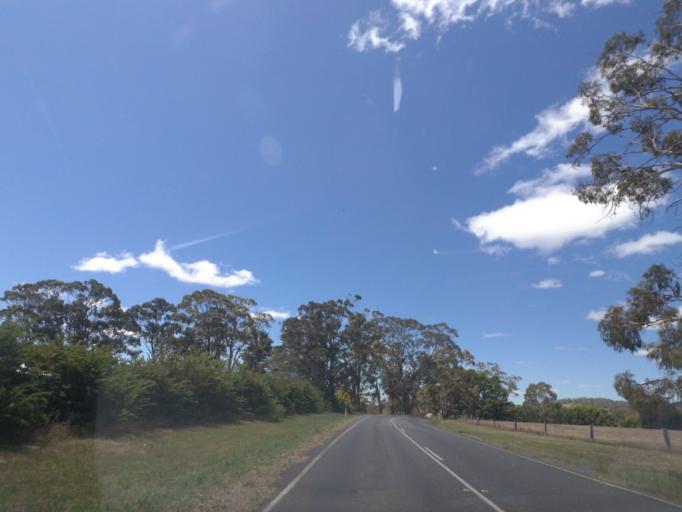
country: AU
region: Victoria
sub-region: Mount Alexander
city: Castlemaine
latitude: -37.2998
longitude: 144.2391
